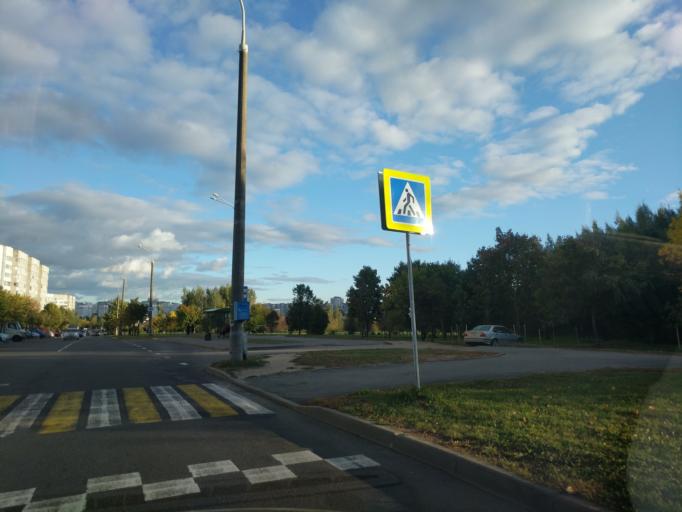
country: BY
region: Minsk
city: Malinovka
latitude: 53.8592
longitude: 27.4523
